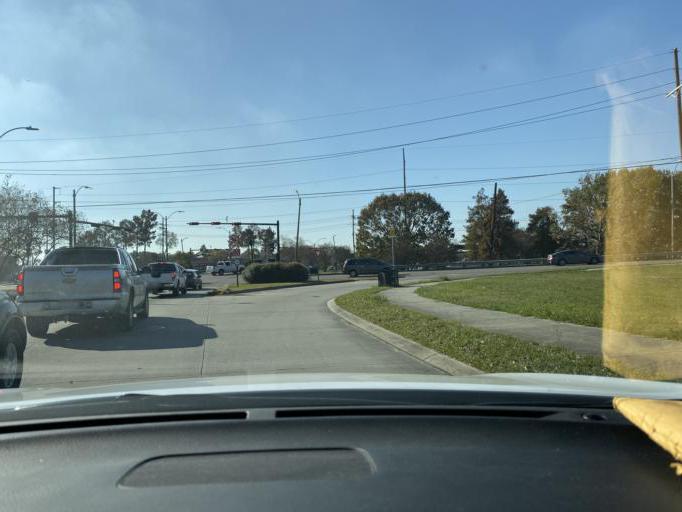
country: US
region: Louisiana
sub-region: Jefferson Parish
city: Terrytown
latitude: 29.9219
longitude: -90.0143
